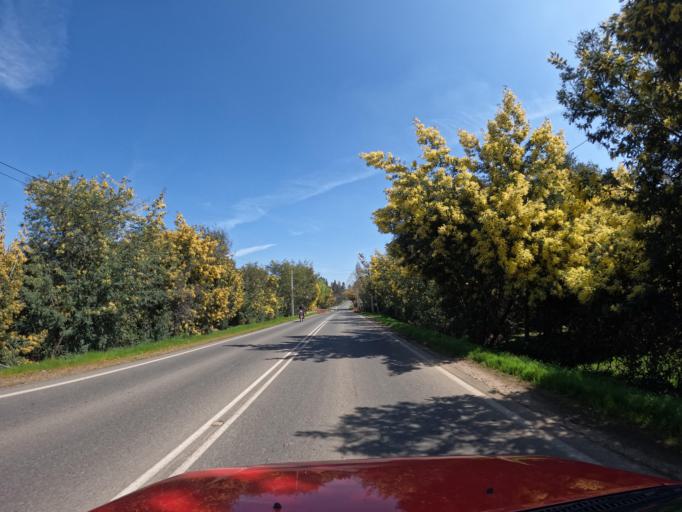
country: CL
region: Maule
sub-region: Provincia de Talca
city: San Clemente
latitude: -35.4890
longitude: -71.2960
